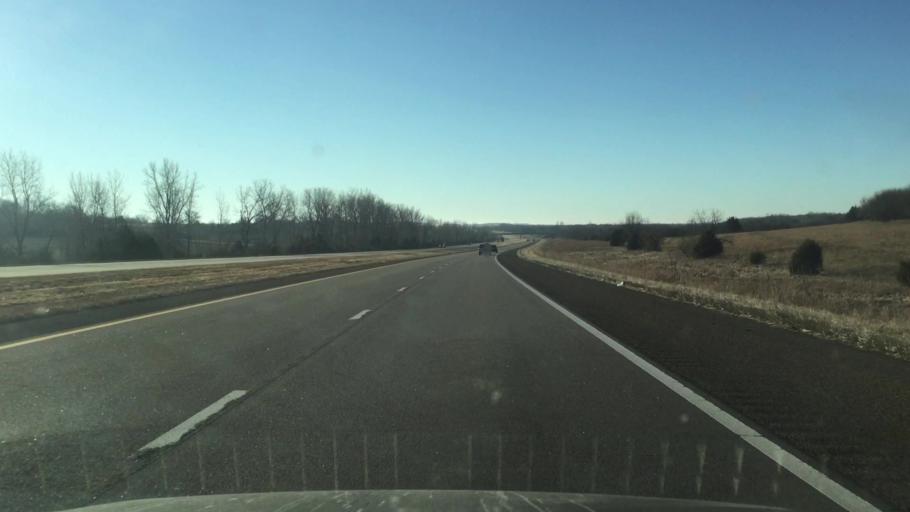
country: US
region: Kansas
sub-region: Johnson County
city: Spring Hill
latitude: 38.7070
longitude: -94.8347
